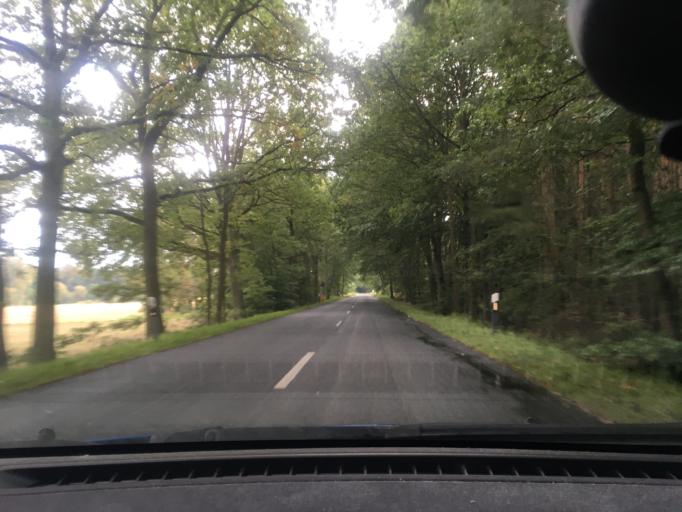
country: DE
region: Lower Saxony
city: Gohrde
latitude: 53.1780
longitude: 10.8771
